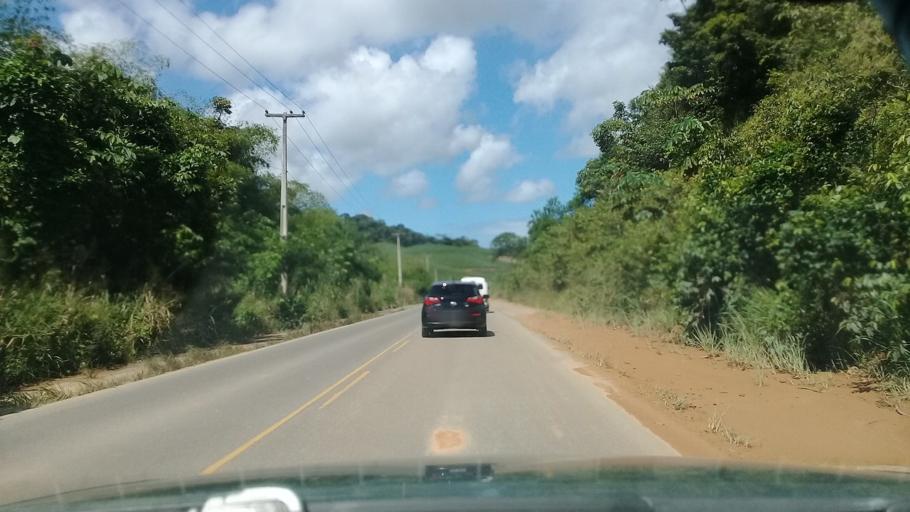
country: BR
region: Pernambuco
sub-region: Ipojuca
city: Ipojuca
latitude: -8.4748
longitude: -35.0927
